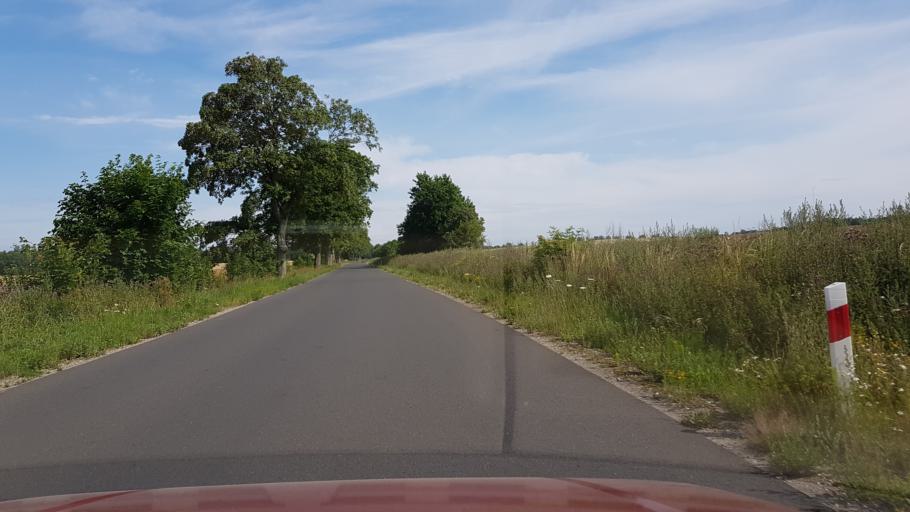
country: PL
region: West Pomeranian Voivodeship
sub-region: Powiat koszalinski
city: Polanow
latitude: 54.1456
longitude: 16.6225
